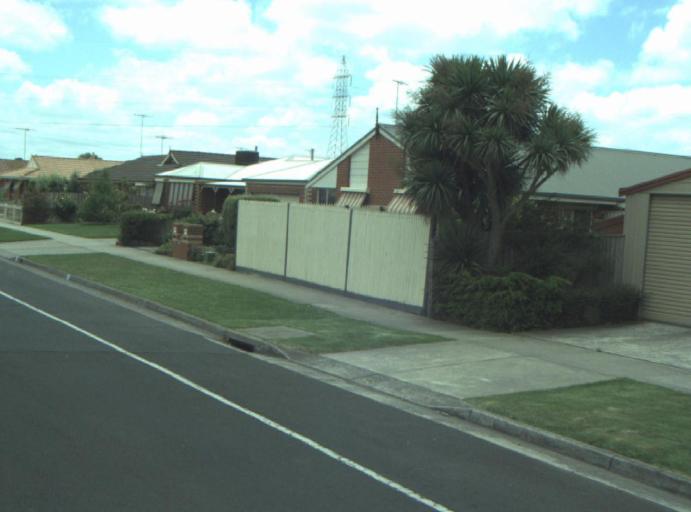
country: AU
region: Victoria
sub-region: Greater Geelong
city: Wandana Heights
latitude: -38.1985
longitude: 144.3272
